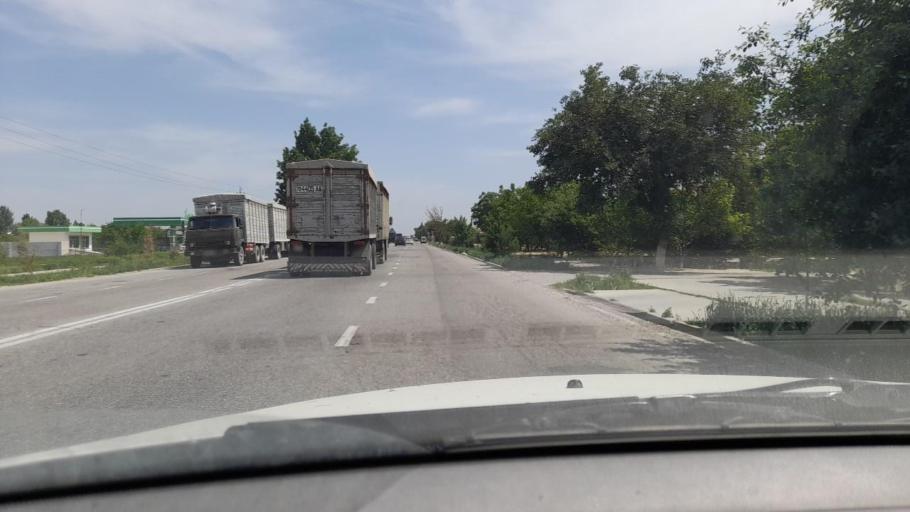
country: UZ
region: Navoiy
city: Karmana Shahri
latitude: 40.1431
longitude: 65.3836
